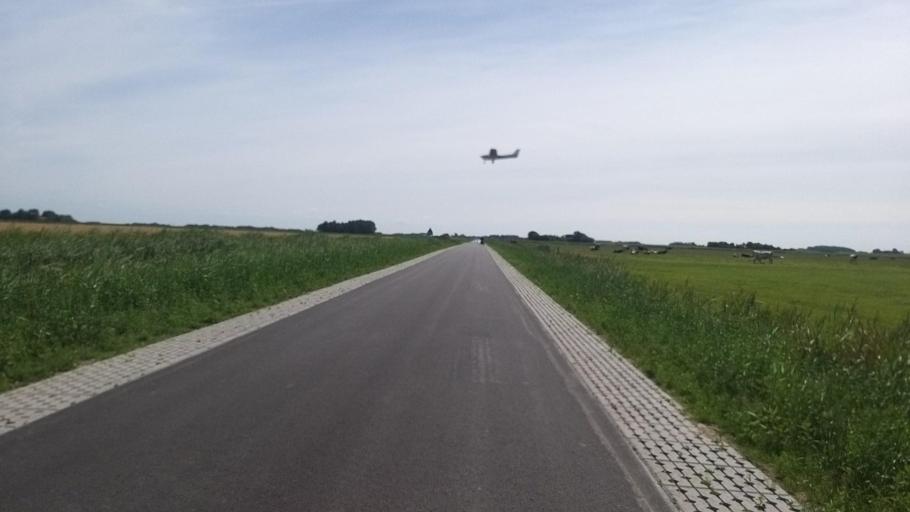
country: NL
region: North Holland
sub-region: Gemeente Texel
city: Den Burg
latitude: 53.1109
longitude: 4.8233
